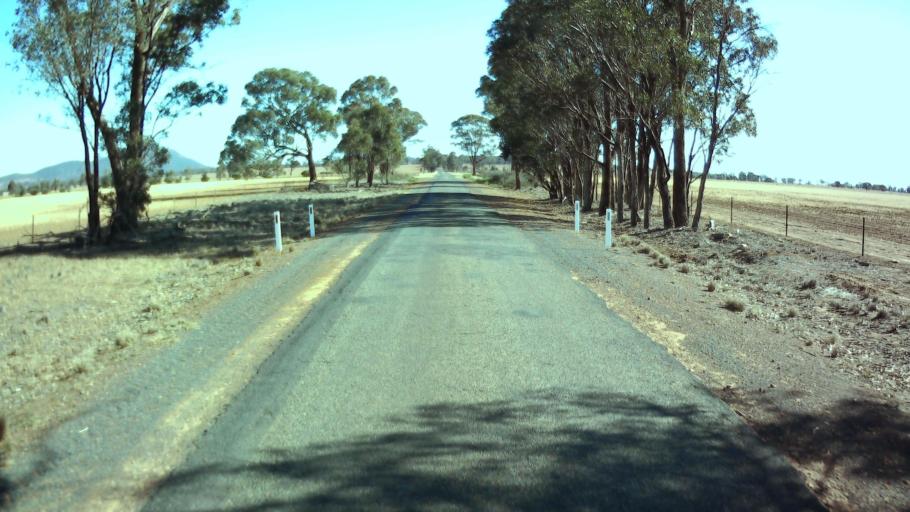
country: AU
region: New South Wales
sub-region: Weddin
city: Grenfell
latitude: -33.8012
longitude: 147.9557
